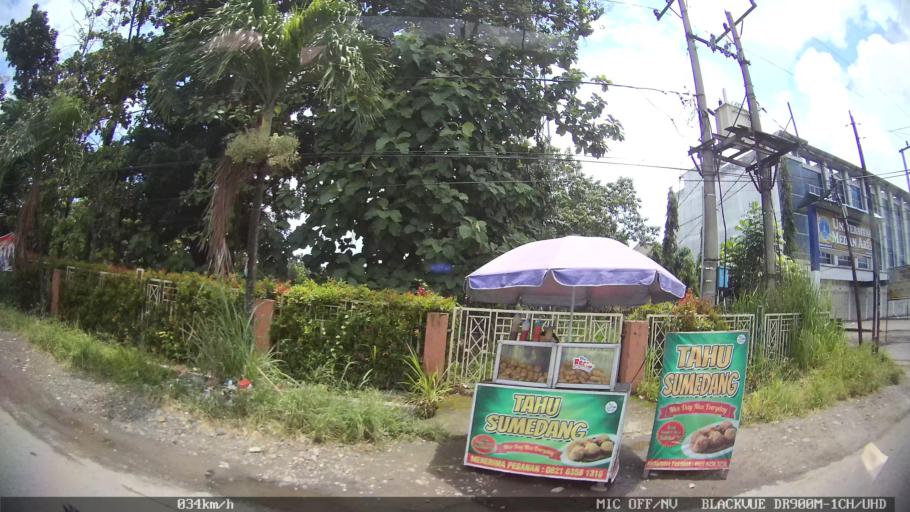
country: ID
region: North Sumatra
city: Medan
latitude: 3.6021
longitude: 98.7119
